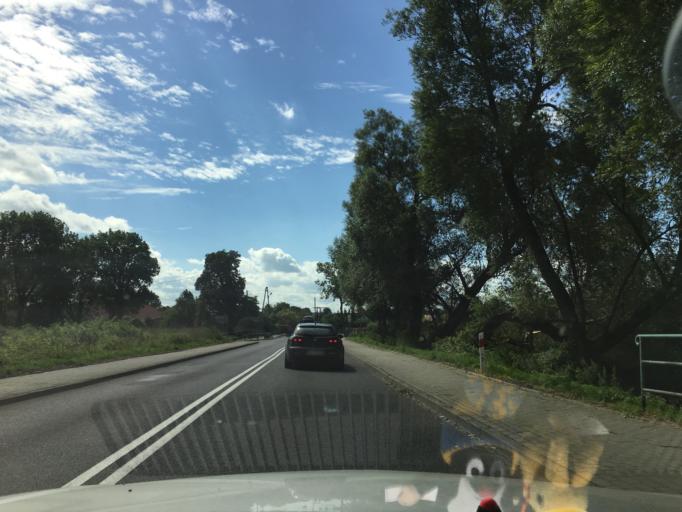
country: PL
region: West Pomeranian Voivodeship
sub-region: Powiat kamienski
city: Kamien Pomorski
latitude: 53.8866
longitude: 14.7893
